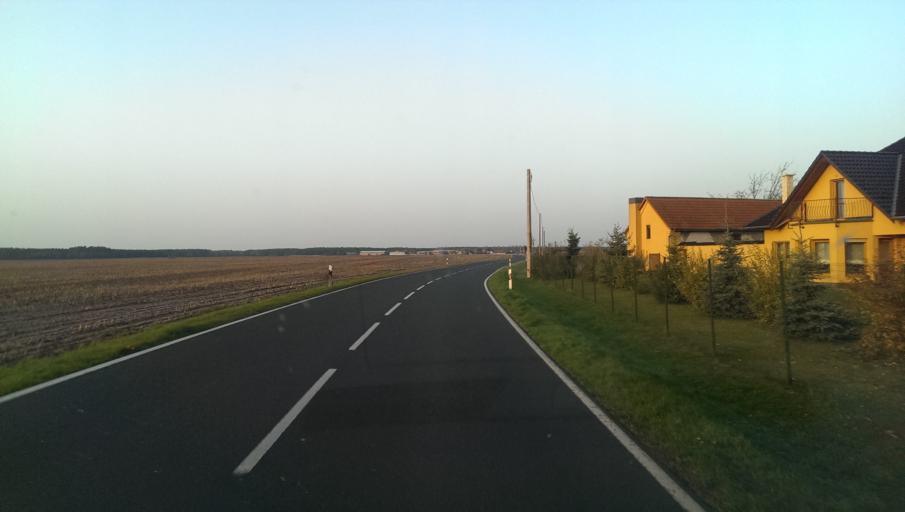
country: DE
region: Saxony-Anhalt
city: Jessen
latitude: 51.8387
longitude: 13.0200
